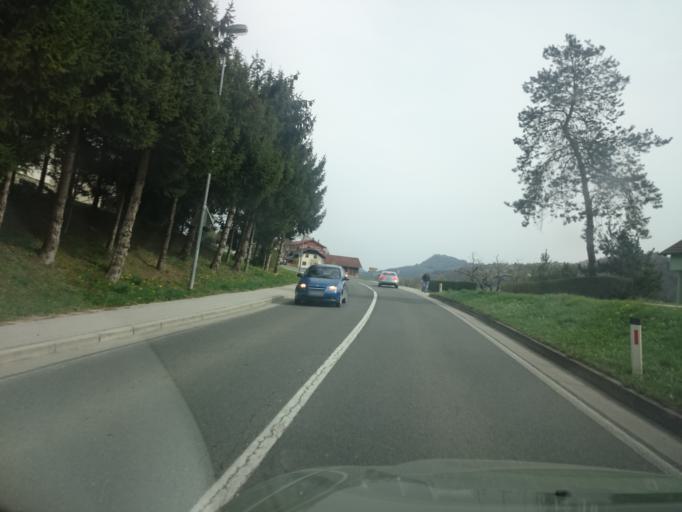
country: SI
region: Store
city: Store
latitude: 46.2193
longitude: 15.3508
